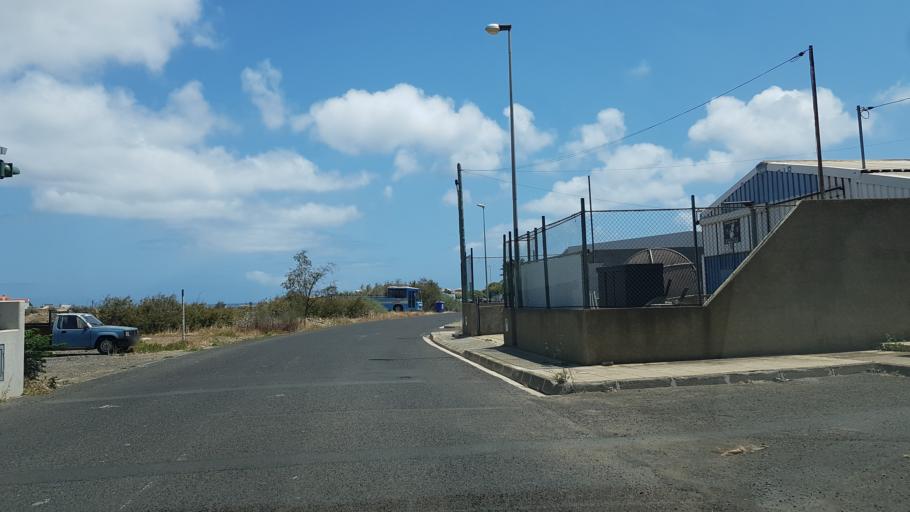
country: PT
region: Madeira
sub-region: Porto Santo
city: Vila de Porto Santo
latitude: 33.0717
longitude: -16.3432
